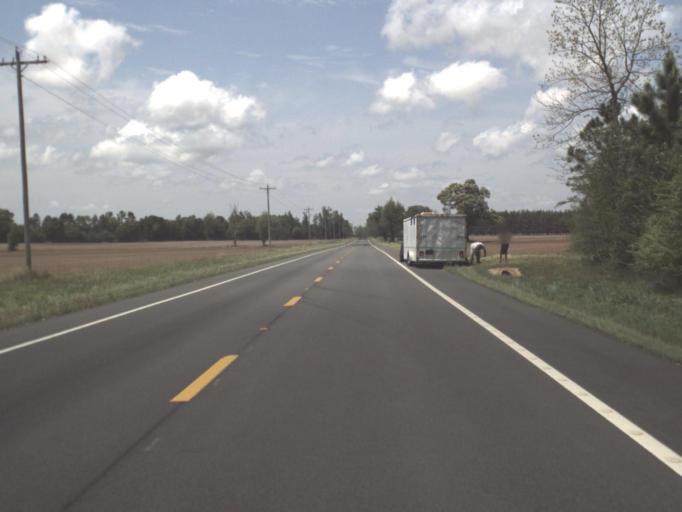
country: US
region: Florida
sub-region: Escambia County
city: Century
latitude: 30.8521
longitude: -87.1497
